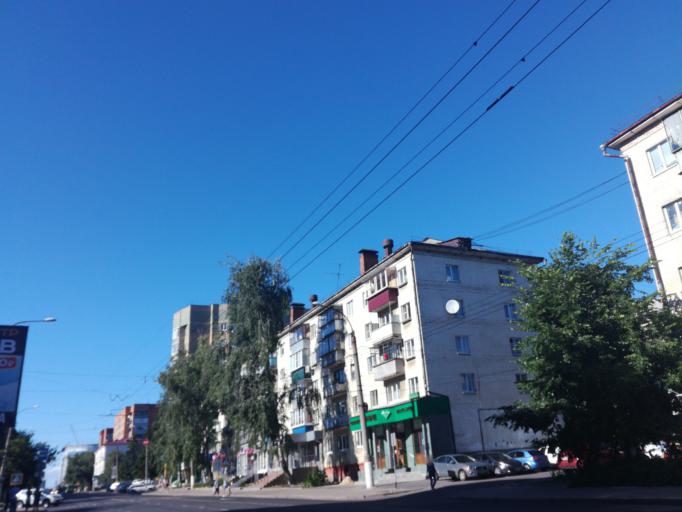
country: RU
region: Kursk
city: Kursk
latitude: 51.7435
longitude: 36.1902
